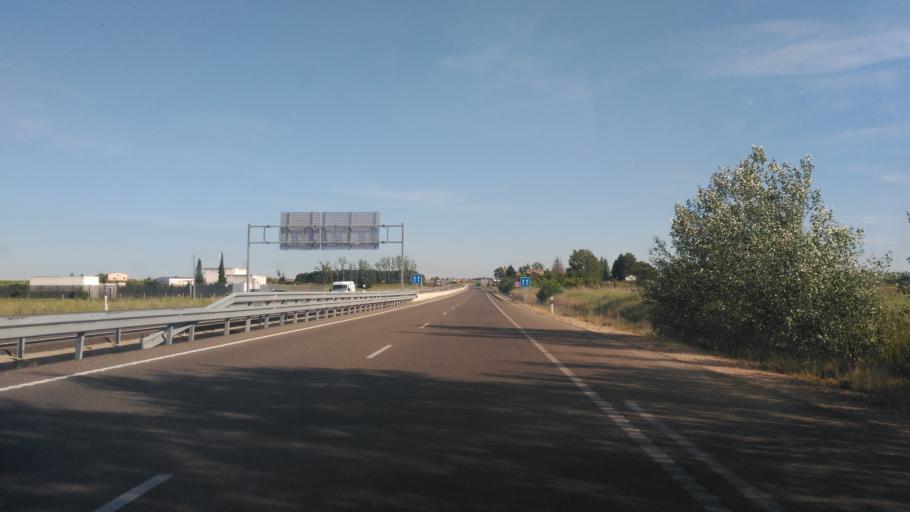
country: ES
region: Castille and Leon
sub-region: Provincia de Zamora
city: Zamora
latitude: 41.4783
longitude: -5.7408
